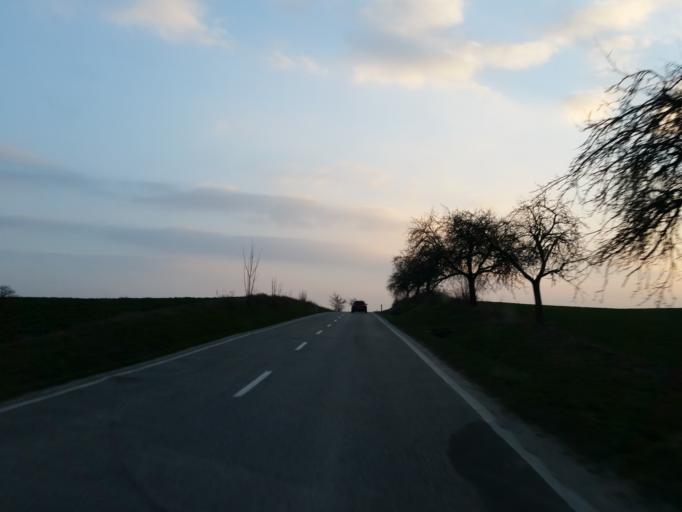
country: SK
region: Nitriansky
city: Banovce nad Bebravou
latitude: 48.5712
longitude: 18.1005
